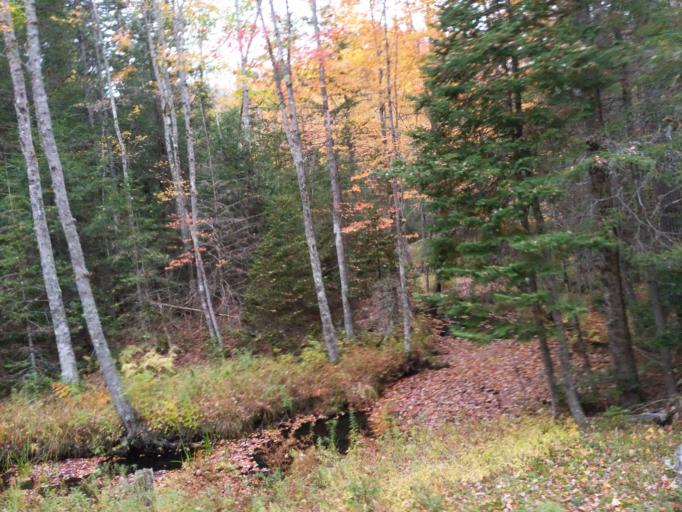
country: US
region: Maine
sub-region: Lincoln County
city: Wiscasset
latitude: 44.0756
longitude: -69.6221
